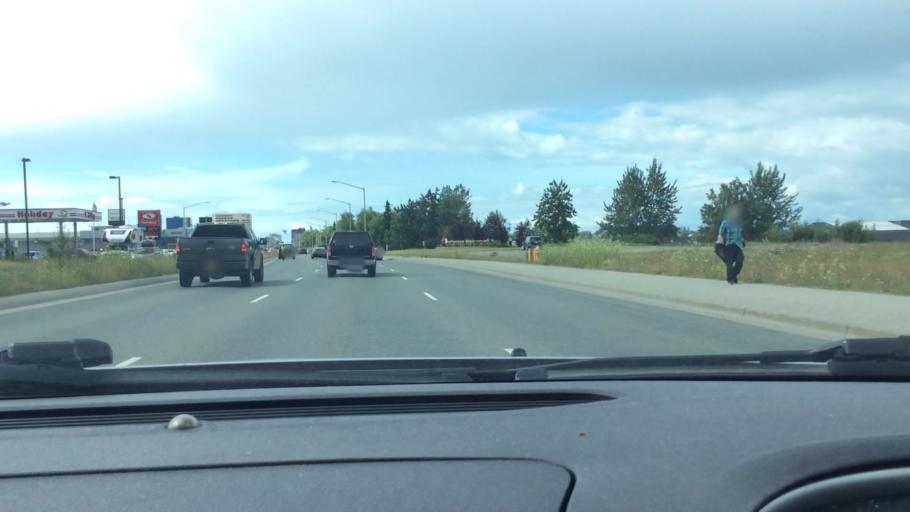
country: US
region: Alaska
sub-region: Anchorage Municipality
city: Anchorage
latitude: 61.2176
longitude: -149.8517
